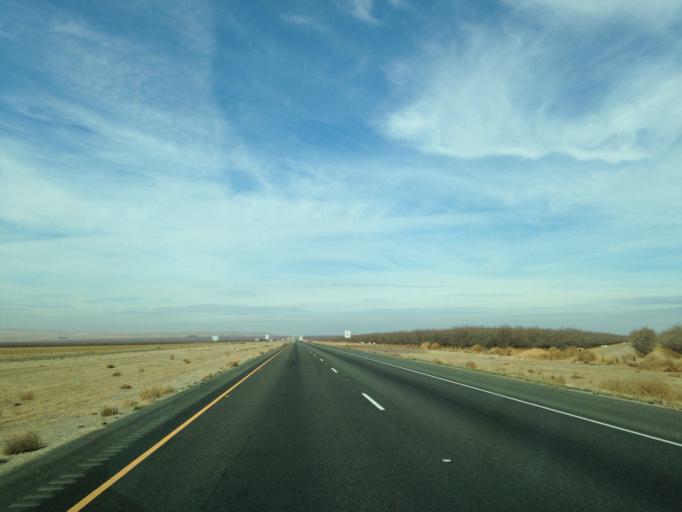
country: US
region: California
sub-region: Merced County
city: South Dos Palos
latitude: 36.7851
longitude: -120.7290
